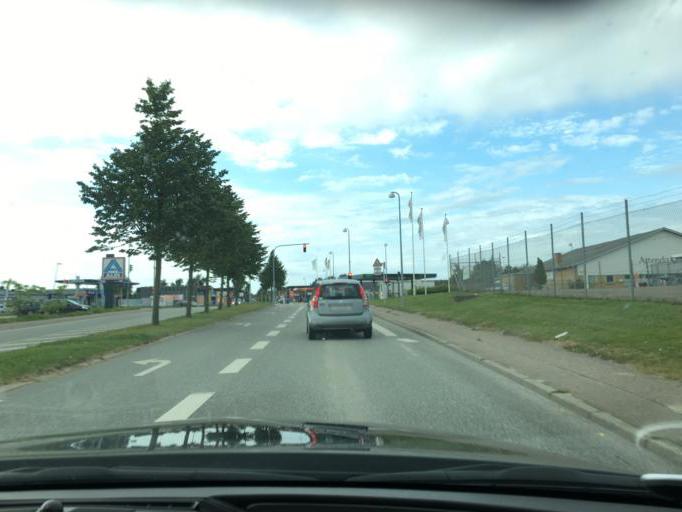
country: DK
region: Capital Region
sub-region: Gribskov Kommune
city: Helsinge
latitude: 56.0152
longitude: 12.1994
